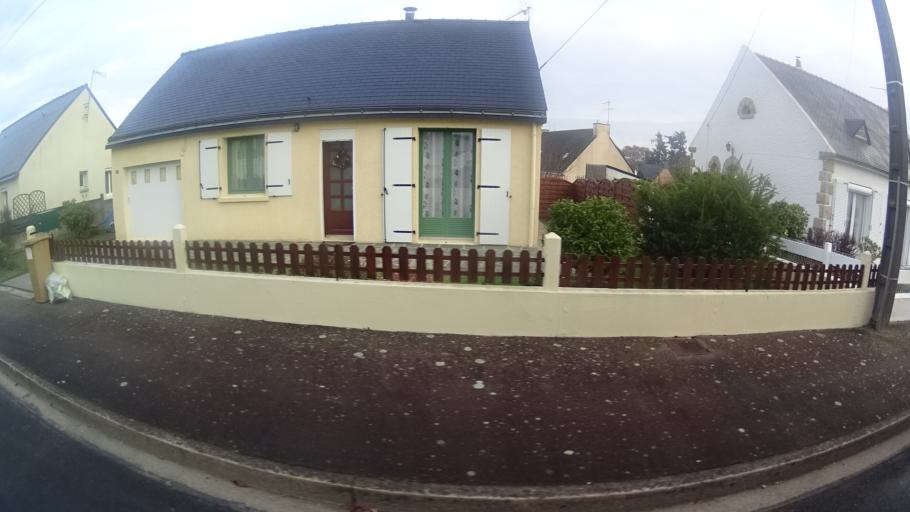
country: FR
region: Pays de la Loire
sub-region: Departement de la Loire-Atlantique
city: Avessac
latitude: 47.6559
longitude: -1.9875
